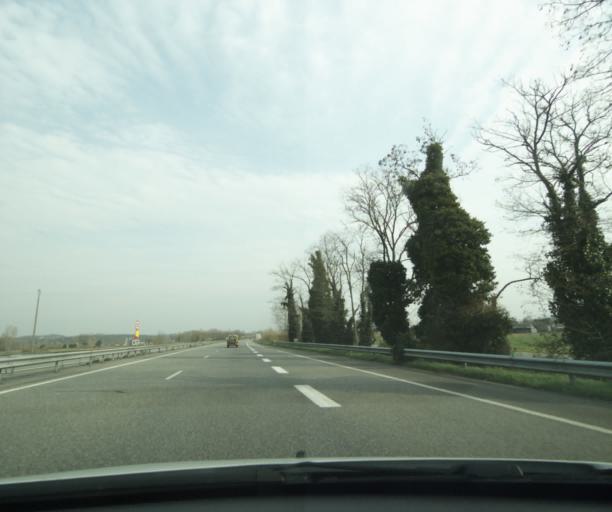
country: FR
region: Aquitaine
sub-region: Departement des Pyrenees-Atlantiques
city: Orthez
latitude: 43.4679
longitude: -0.7420
